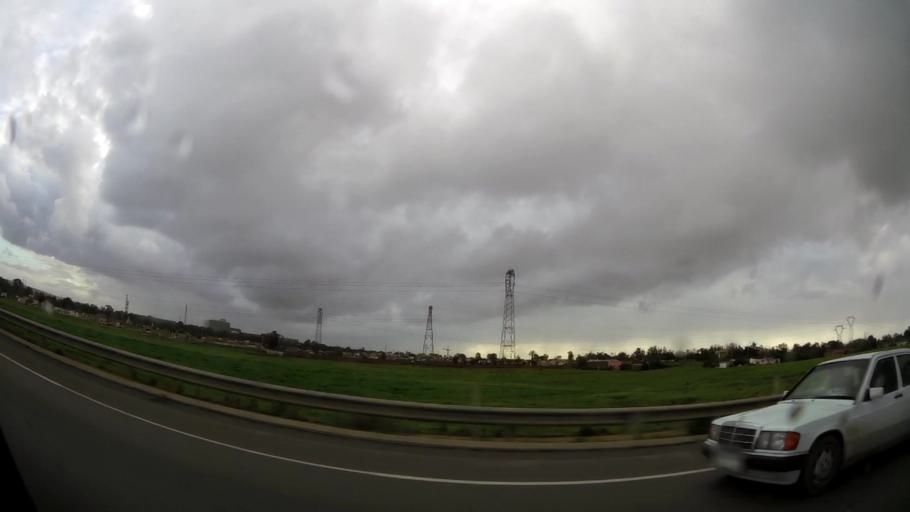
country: MA
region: Grand Casablanca
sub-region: Mohammedia
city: Mohammedia
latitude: 33.6416
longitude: -7.4217
